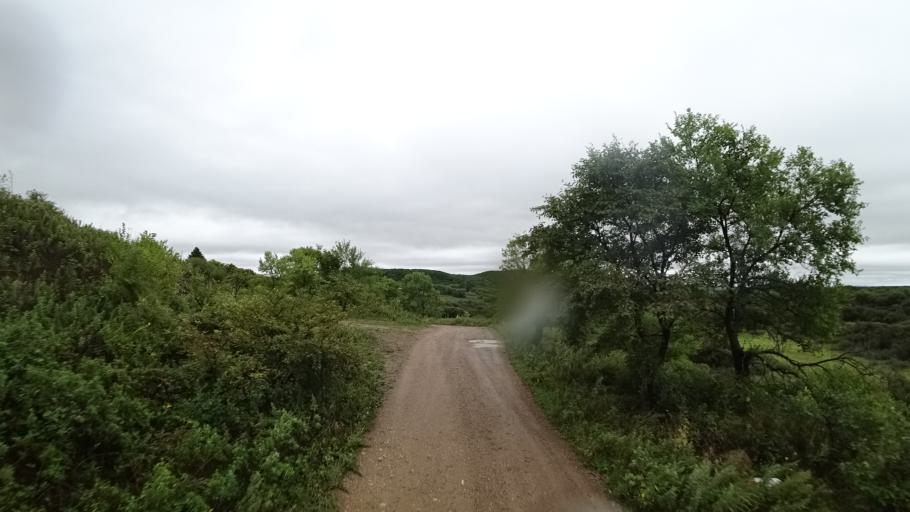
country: RU
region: Primorskiy
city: Monastyrishche
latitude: 44.2593
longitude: 132.4085
